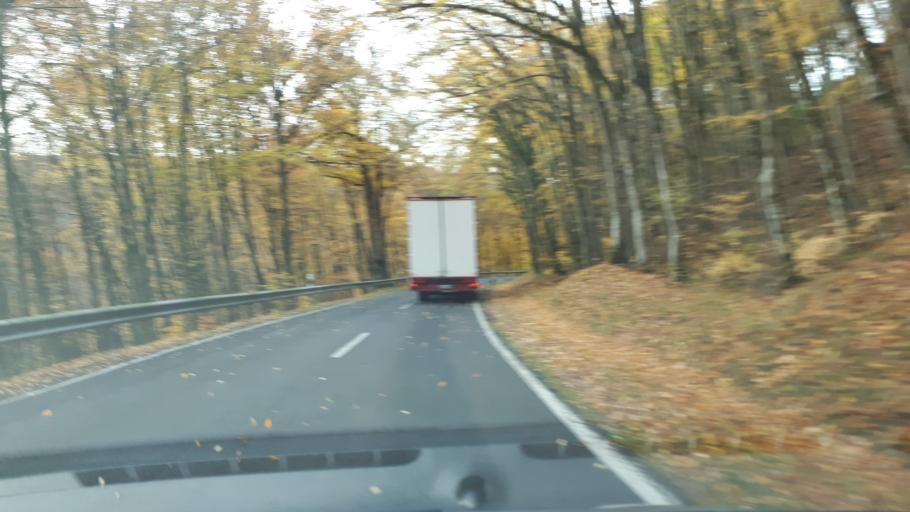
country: DE
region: Rheinland-Pfalz
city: Bad Bertrich
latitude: 50.0792
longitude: 7.0213
